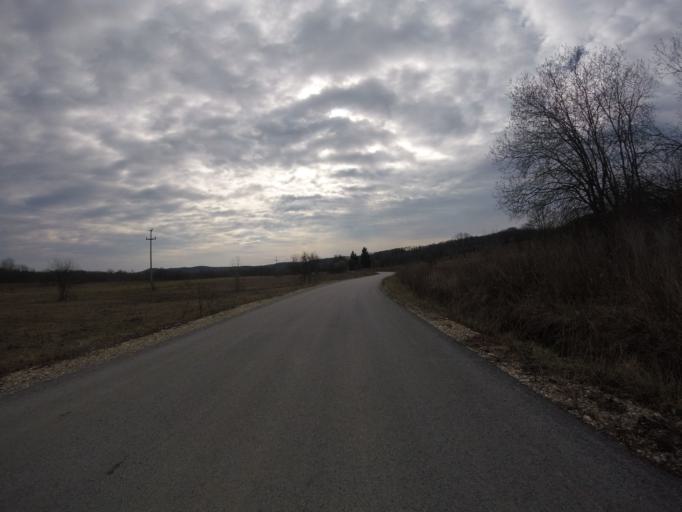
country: HR
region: Sisacko-Moslavacka
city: Glina
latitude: 45.4424
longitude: 16.0730
